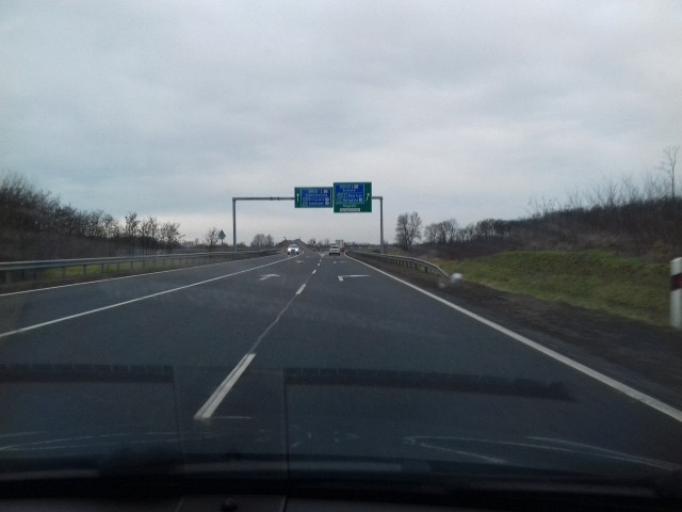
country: HU
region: Szabolcs-Szatmar-Bereg
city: Nagykallo
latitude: 47.9026
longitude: 21.8173
